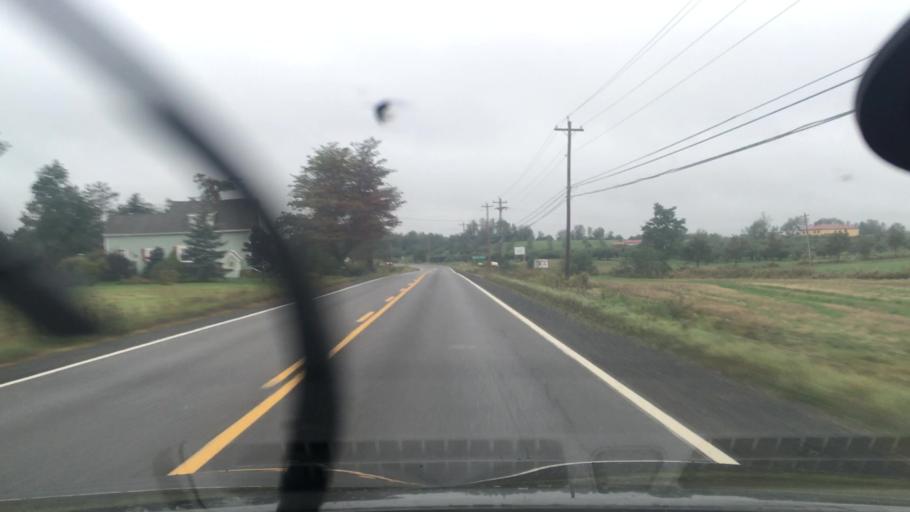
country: CA
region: Nova Scotia
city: Windsor
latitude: 44.9507
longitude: -64.1695
